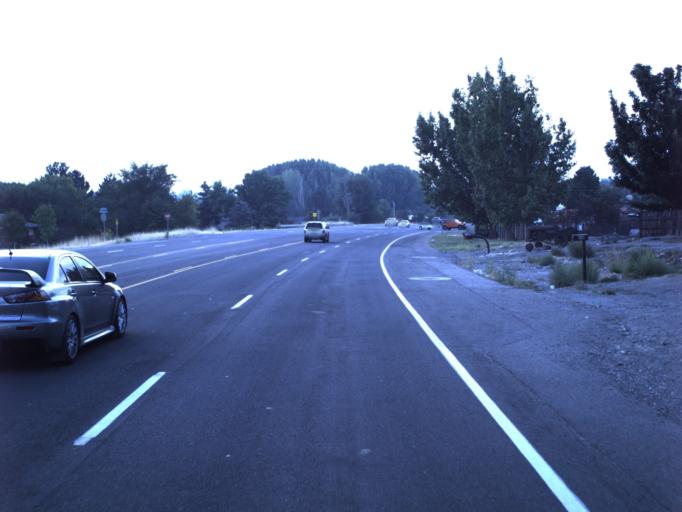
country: US
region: Utah
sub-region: Utah County
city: Springville
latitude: 40.1434
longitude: -111.6018
